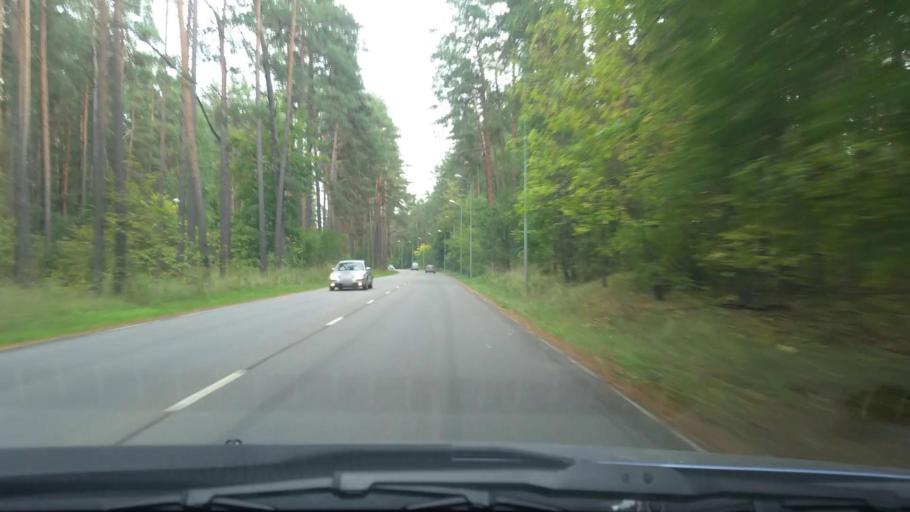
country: LV
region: Riga
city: Jaunciems
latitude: 56.9781
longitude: 24.2157
